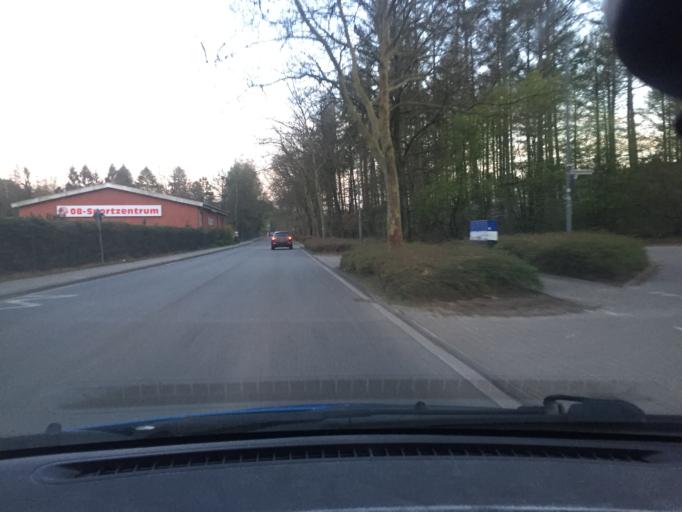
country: DE
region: Lower Saxony
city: Buchholz in der Nordheide
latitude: 53.3155
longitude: 9.8635
